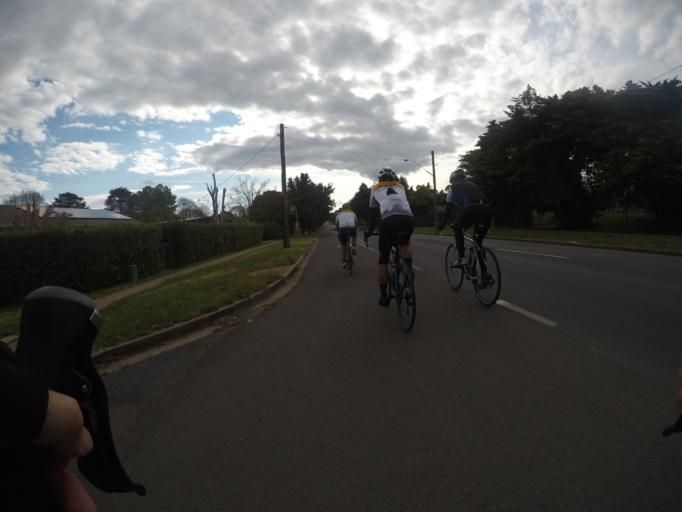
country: AU
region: New South Wales
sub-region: Orange Municipality
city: Orange
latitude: -33.2813
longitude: 149.0830
